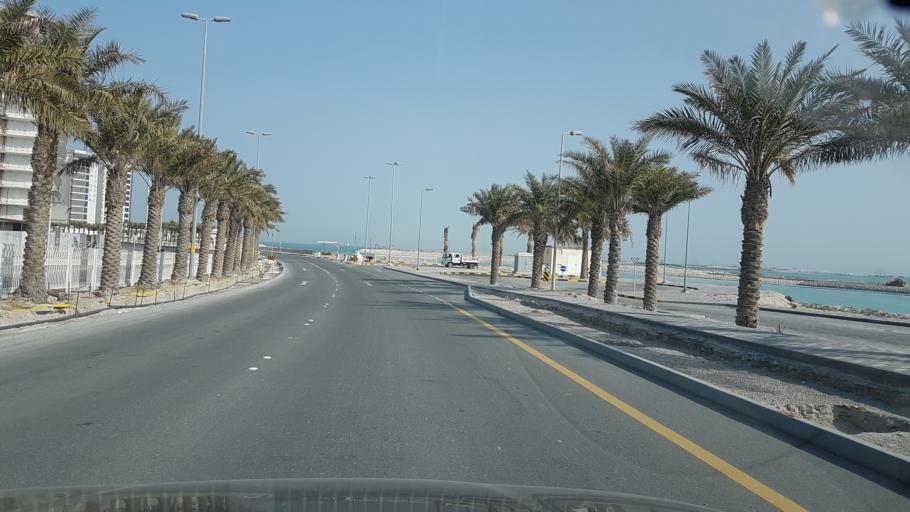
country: BH
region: Muharraq
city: Al Hadd
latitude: 26.2685
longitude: 50.6725
